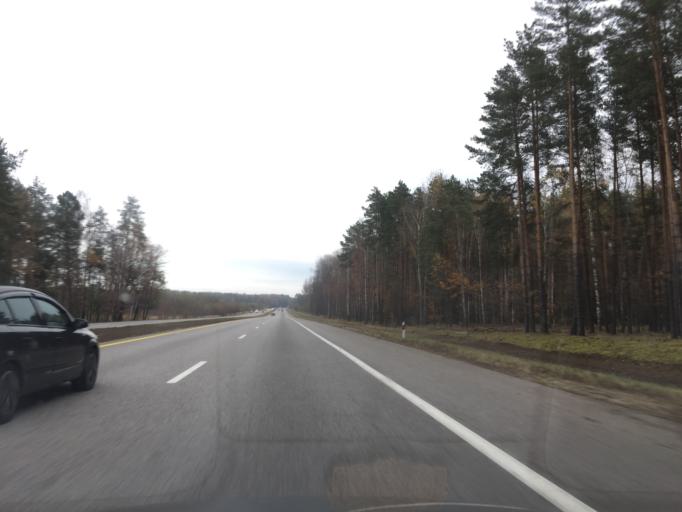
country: BY
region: Gomel
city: Gomel
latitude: 52.3661
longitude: 30.7433
